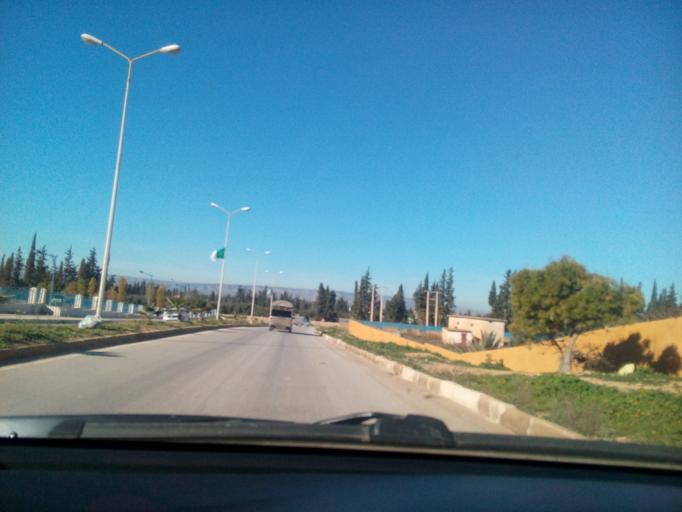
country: DZ
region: Relizane
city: Relizane
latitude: 35.7237
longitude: 0.5268
